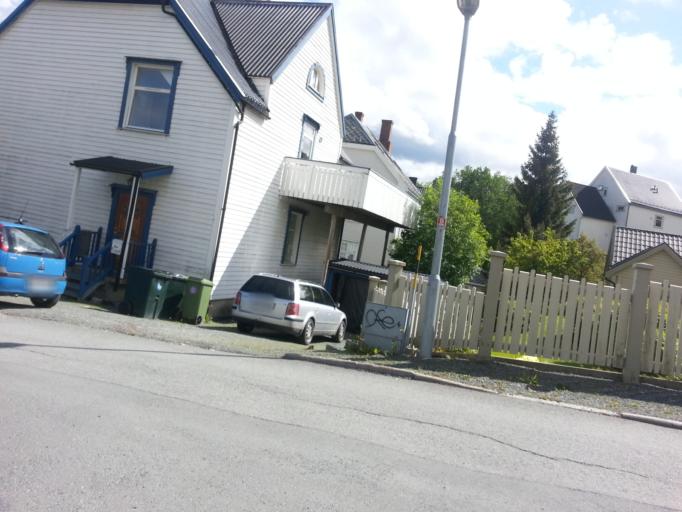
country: NO
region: Sor-Trondelag
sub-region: Trondheim
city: Trondheim
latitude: 63.4137
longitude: 10.3811
